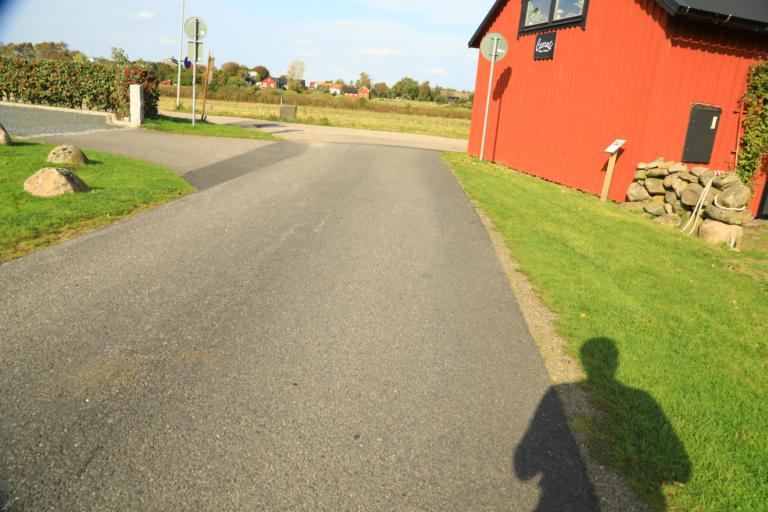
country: SE
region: Halland
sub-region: Varbergs Kommun
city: Varberg
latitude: 57.1185
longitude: 12.2131
